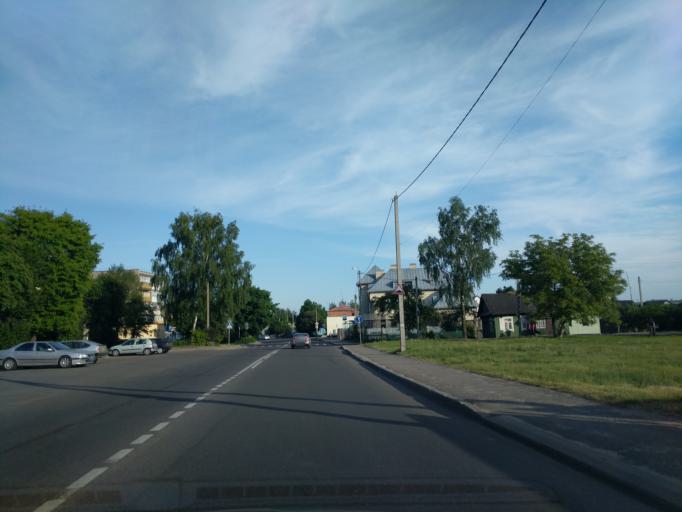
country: BY
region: Grodnenskaya
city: Ashmyany
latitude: 54.4247
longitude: 25.9293
